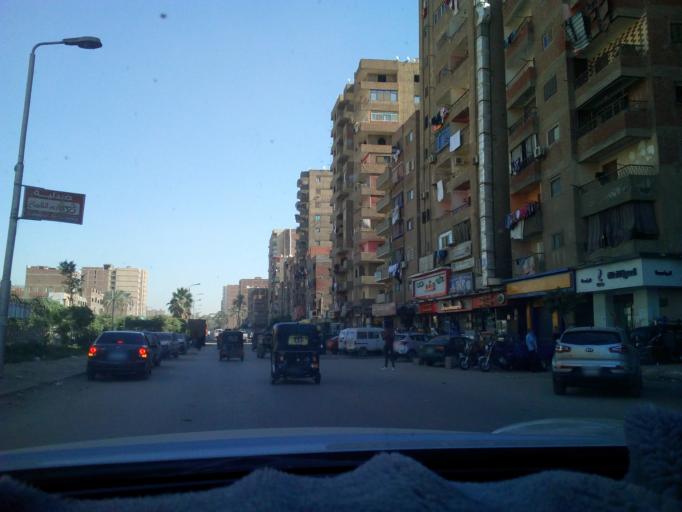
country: EG
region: Muhafazat al Qalyubiyah
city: Al Khankah
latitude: 30.1412
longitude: 31.3436
